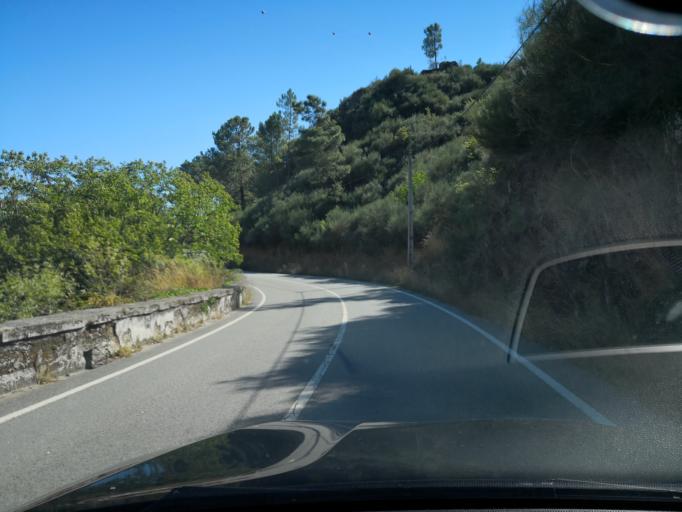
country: PT
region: Vila Real
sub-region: Vila Real
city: Vila Real
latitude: 41.2673
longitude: -7.7783
